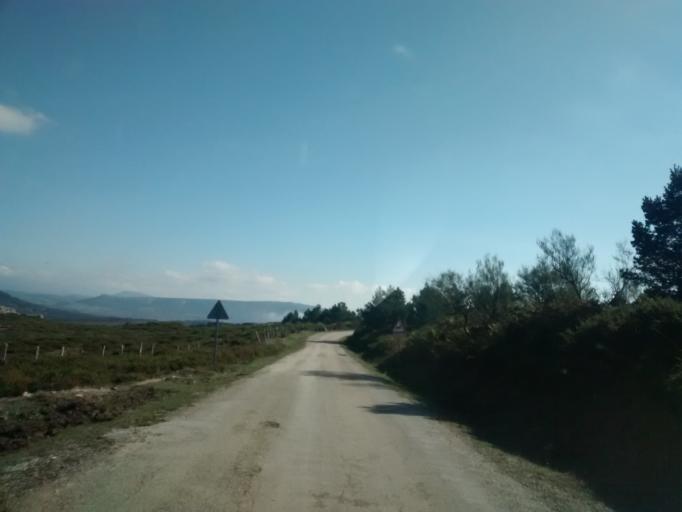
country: ES
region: Castille and Leon
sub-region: Provincia de Burgos
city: Arija
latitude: 42.9311
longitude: -3.9617
